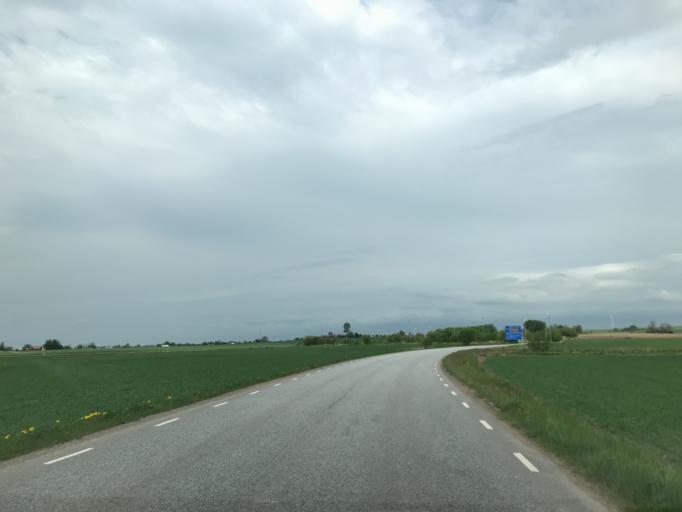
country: SE
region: Skane
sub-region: Svalovs Kommun
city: Svaloev
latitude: 55.8733
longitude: 13.1580
